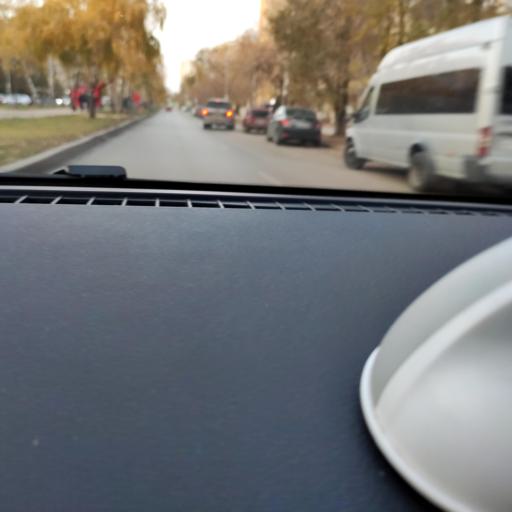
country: RU
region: Samara
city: Samara
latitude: 53.1922
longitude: 50.1792
